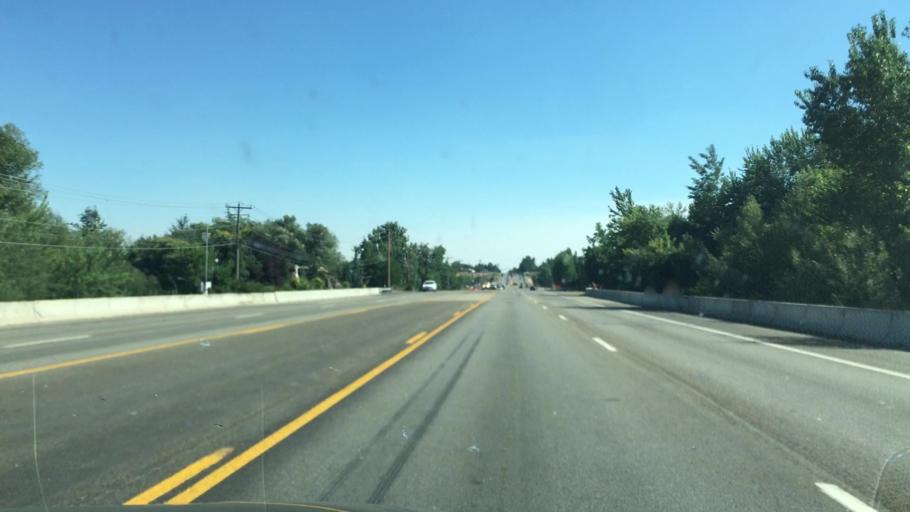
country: US
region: Idaho
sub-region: Ada County
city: Eagle
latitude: 43.6758
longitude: -116.3543
